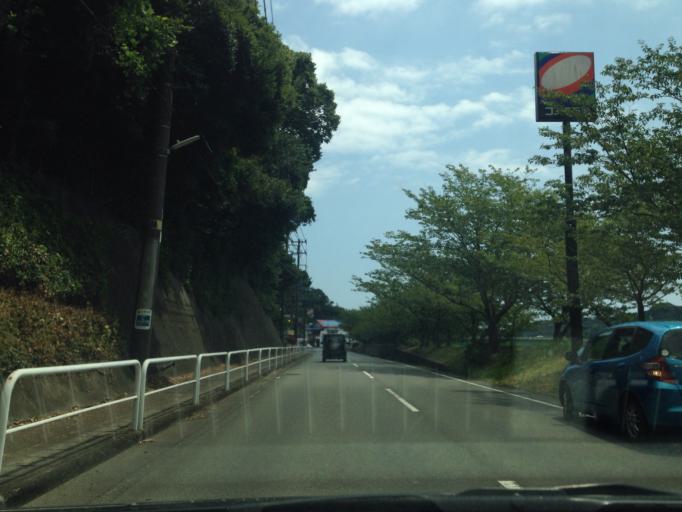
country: JP
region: Shizuoka
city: Shimoda
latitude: 34.6442
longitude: 138.8861
